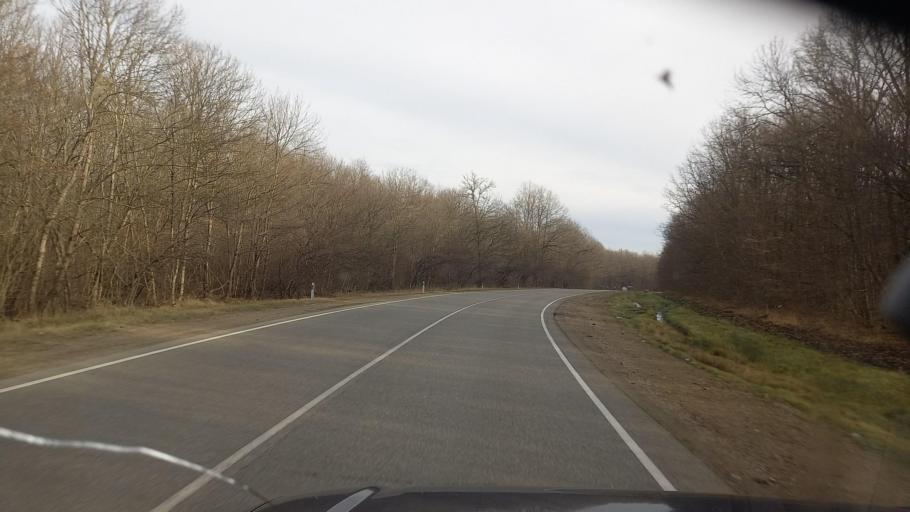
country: RU
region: Krasnodarskiy
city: Khadyzhensk
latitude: 44.6376
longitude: 39.5125
